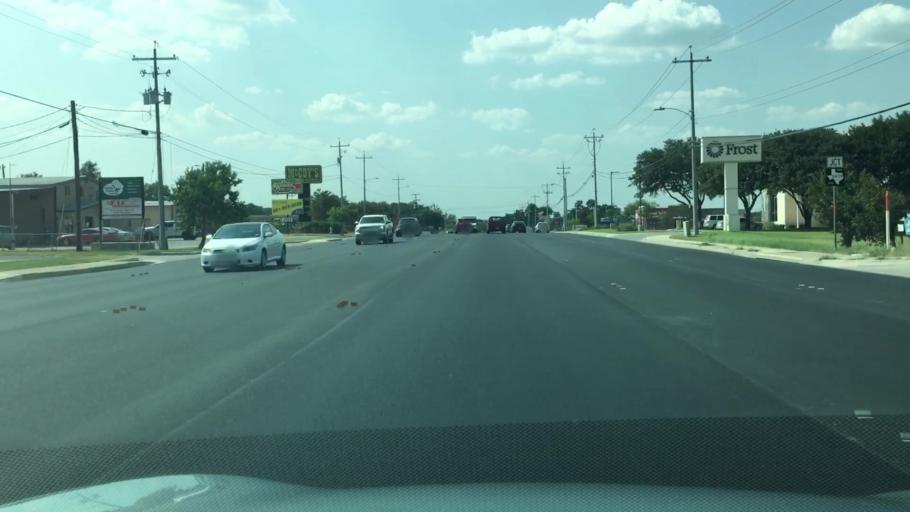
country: US
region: Texas
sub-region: Hays County
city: San Marcos
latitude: 29.8633
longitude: -97.9605
